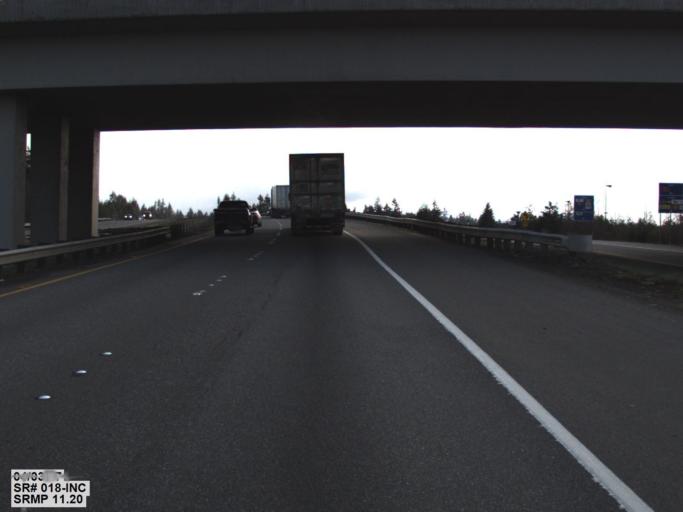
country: US
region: Washington
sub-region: King County
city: Covington
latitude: 47.3557
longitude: -122.1243
